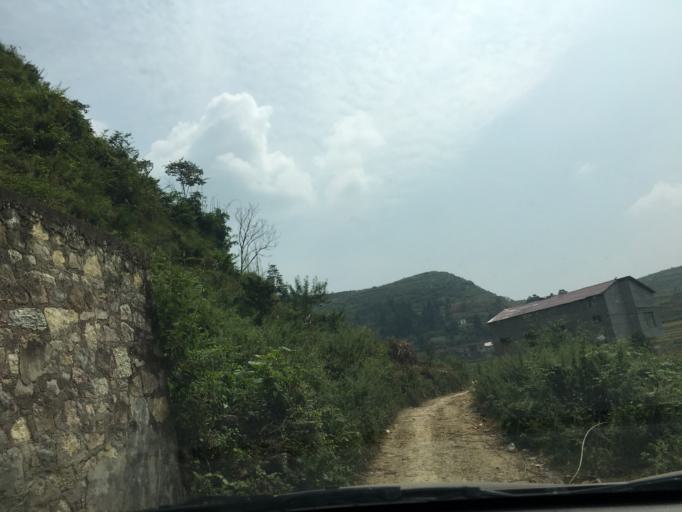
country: CN
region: Guizhou Sheng
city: Anshun
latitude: 25.5962
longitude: 105.6706
